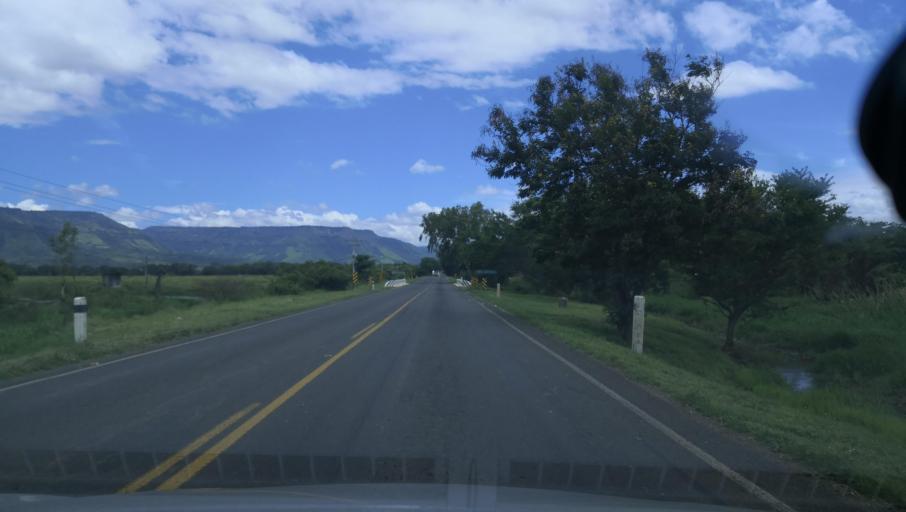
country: NI
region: Matagalpa
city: Ciudad Dario
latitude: 12.9012
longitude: -86.1639
